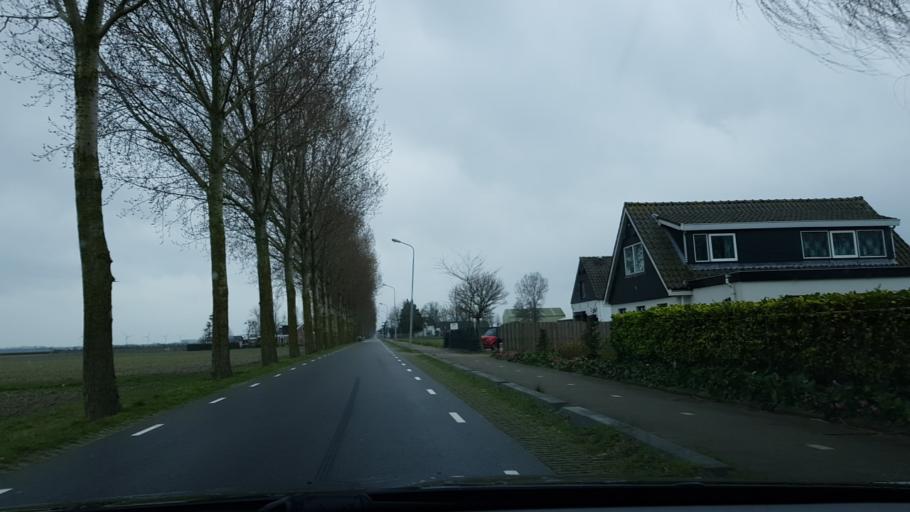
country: NL
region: North Holland
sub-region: Gemeente Haarlemmermeer
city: Hoofddorp
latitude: 52.2692
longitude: 4.6805
